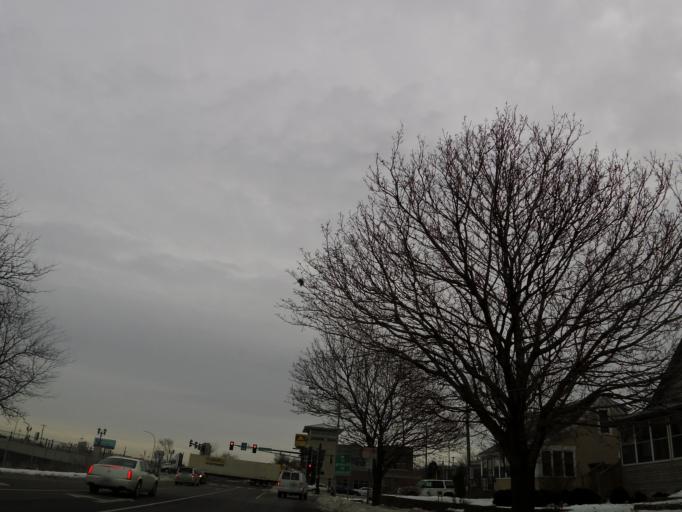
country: US
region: Minnesota
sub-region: Ramsey County
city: Falcon Heights
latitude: 44.9512
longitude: -93.1683
